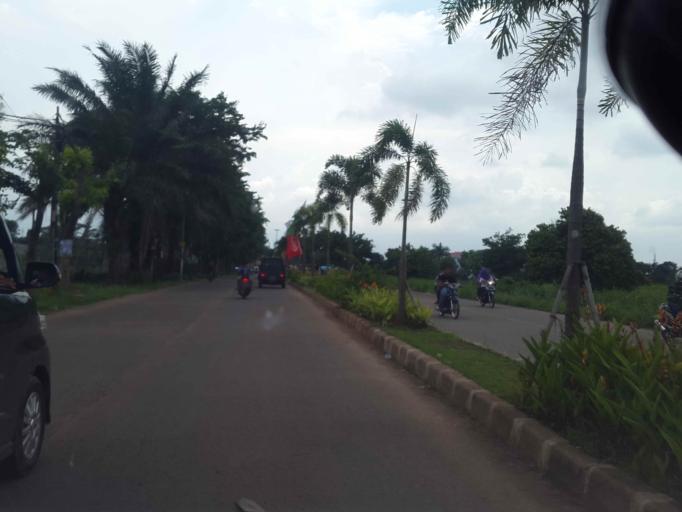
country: ID
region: West Java
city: Cileungsir
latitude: -6.3432
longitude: 106.9439
